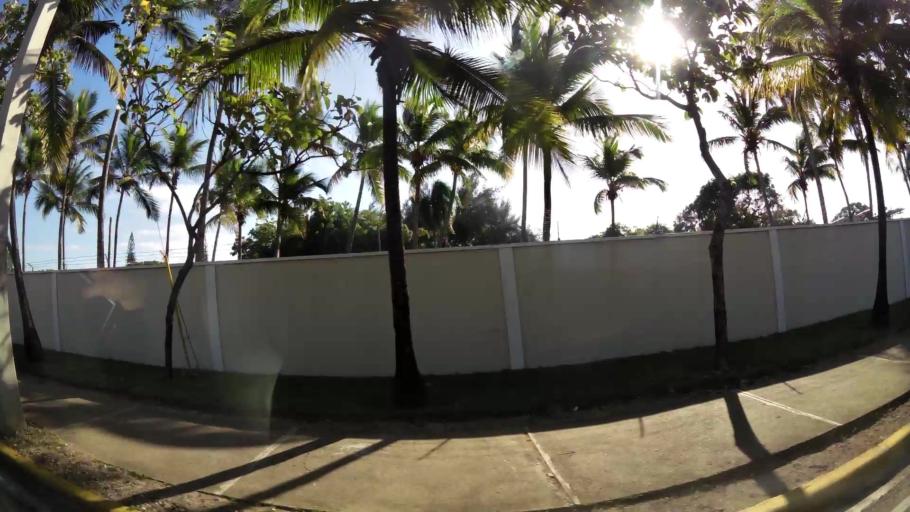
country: DO
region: Nacional
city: Ciudad Nueva
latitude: 18.4701
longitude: -69.8748
